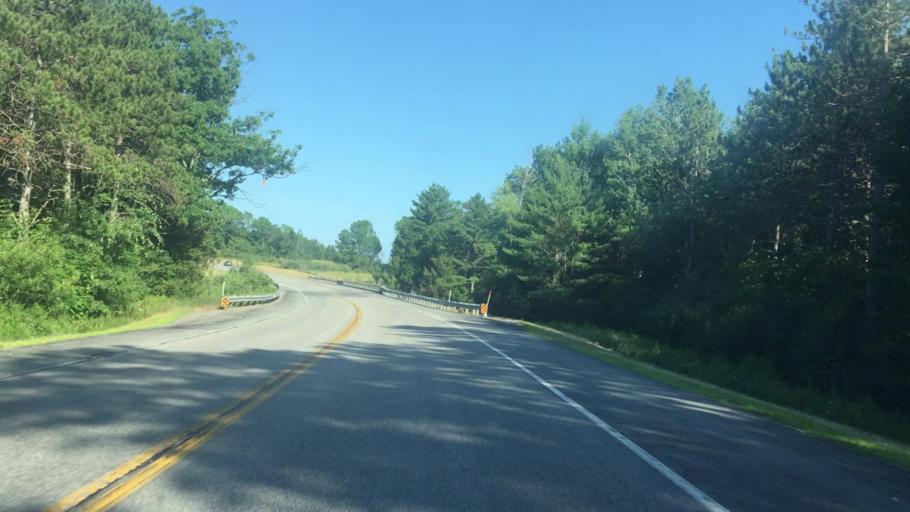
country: US
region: Maine
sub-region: Cumberland County
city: Gorham
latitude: 43.6492
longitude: -70.4447
